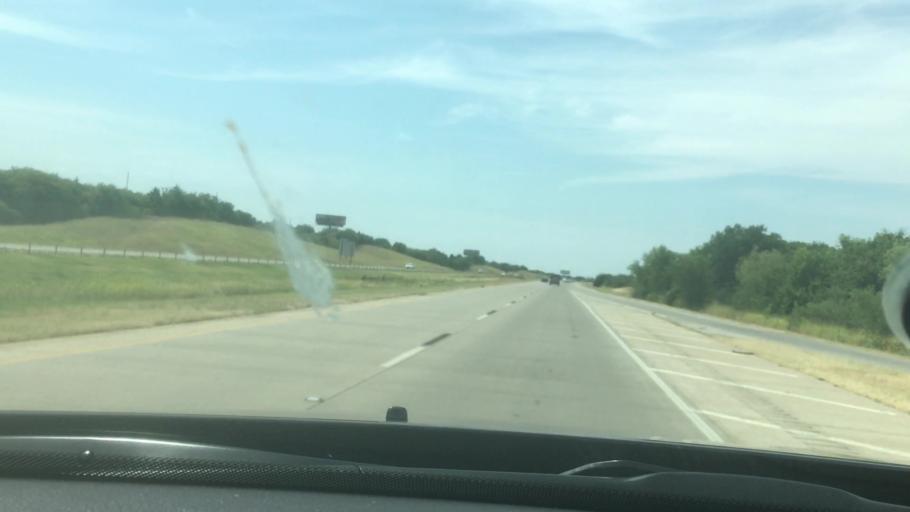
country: US
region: Oklahoma
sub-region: Carter County
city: Ardmore
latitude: 34.3011
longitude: -97.1599
